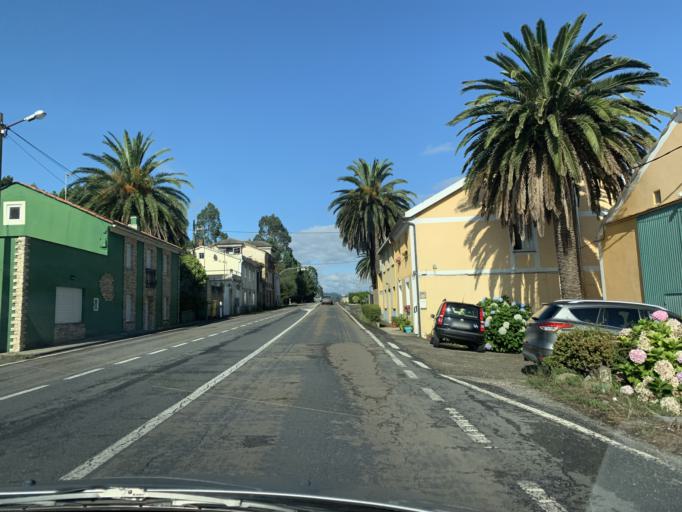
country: ES
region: Galicia
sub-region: Provincia de Lugo
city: Barreiros
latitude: 43.5446
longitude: -7.2181
